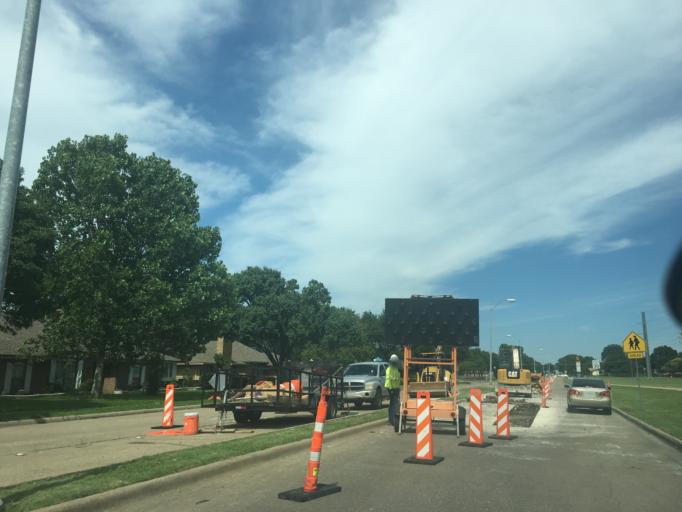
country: US
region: Texas
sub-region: Dallas County
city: Richardson
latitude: 32.9386
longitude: -96.7079
